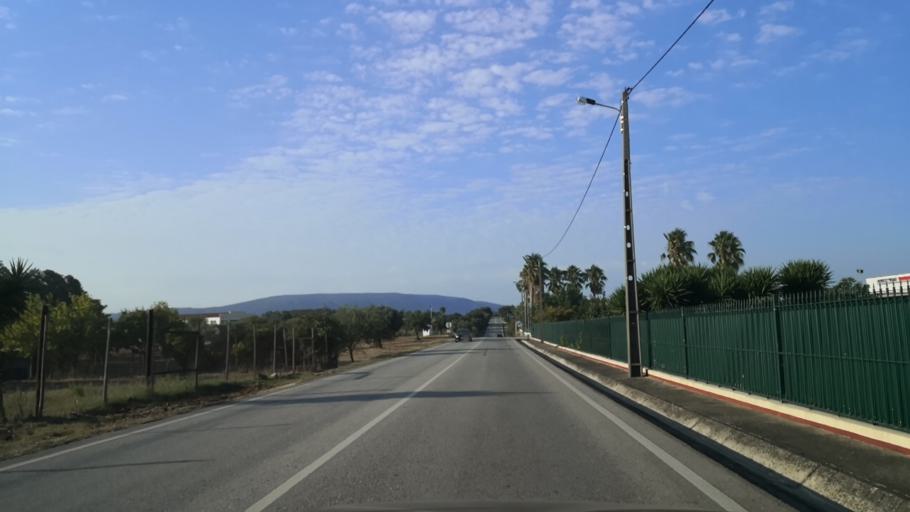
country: PT
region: Santarem
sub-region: Alcanena
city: Alcanena
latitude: 39.4187
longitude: -8.6362
